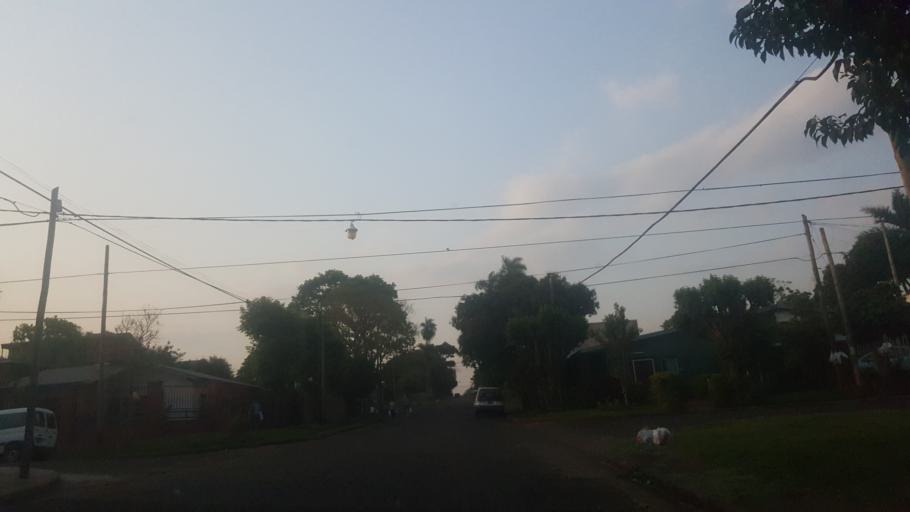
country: AR
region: Misiones
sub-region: Departamento de Capital
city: Posadas
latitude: -27.4012
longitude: -55.9108
